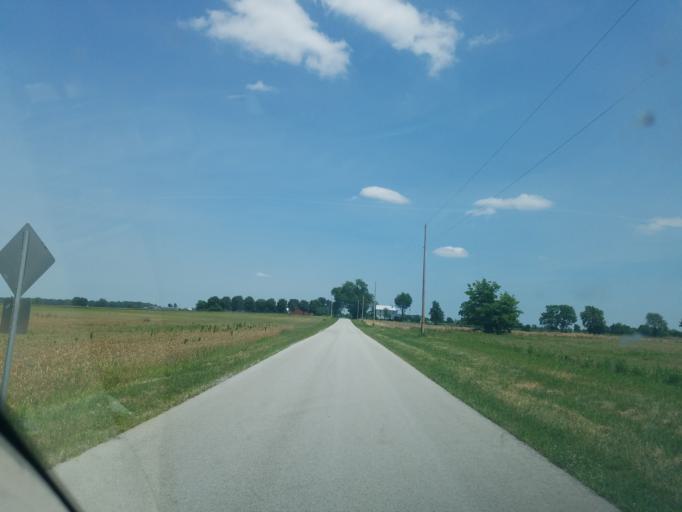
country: US
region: Ohio
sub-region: Wyandot County
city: Carey
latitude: 40.9476
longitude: -83.5032
